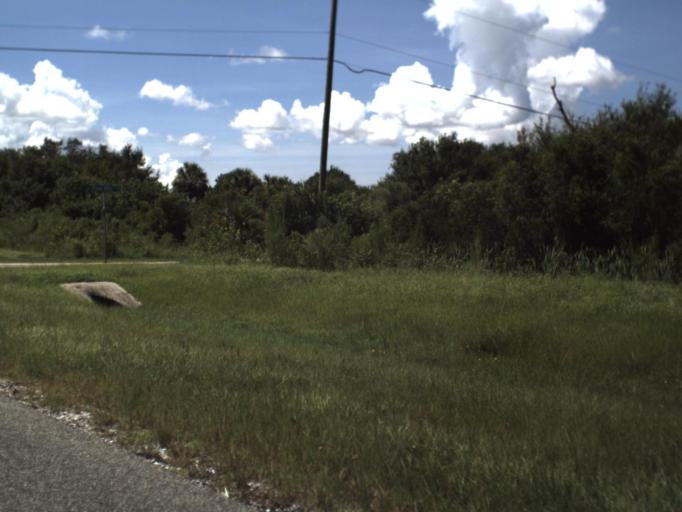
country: US
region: Florida
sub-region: Charlotte County
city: Harbour Heights
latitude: 27.0154
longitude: -81.9588
